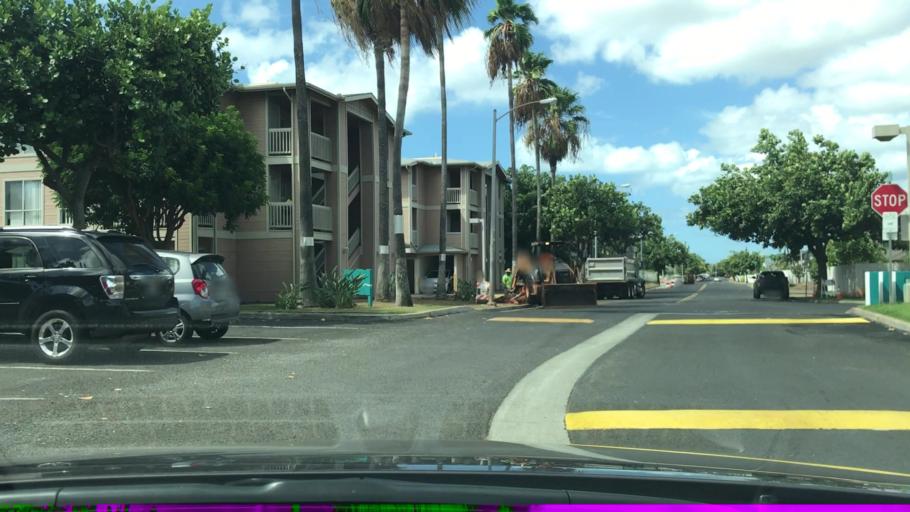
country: US
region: Hawaii
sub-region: Honolulu County
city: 'Ewa Gentry
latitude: 21.3356
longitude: -158.0250
